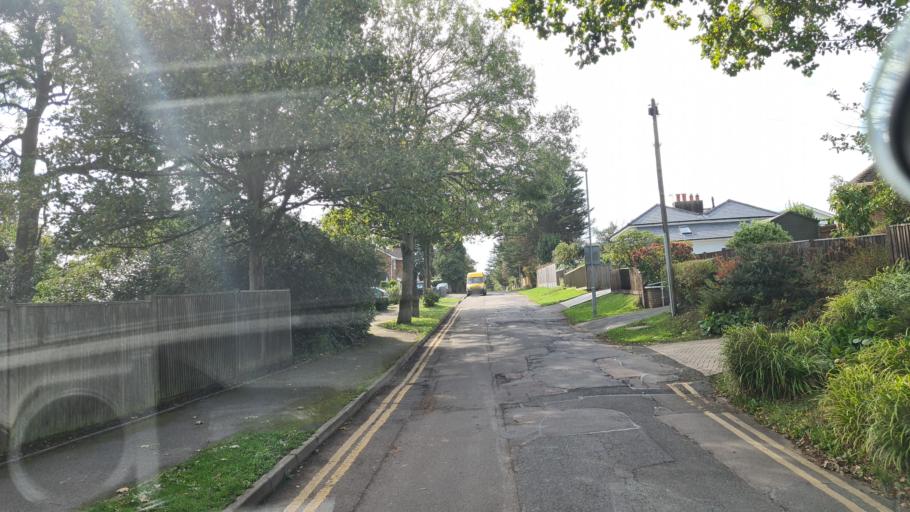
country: GB
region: England
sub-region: East Sussex
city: Hastings
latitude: 50.8787
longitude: 0.5611
